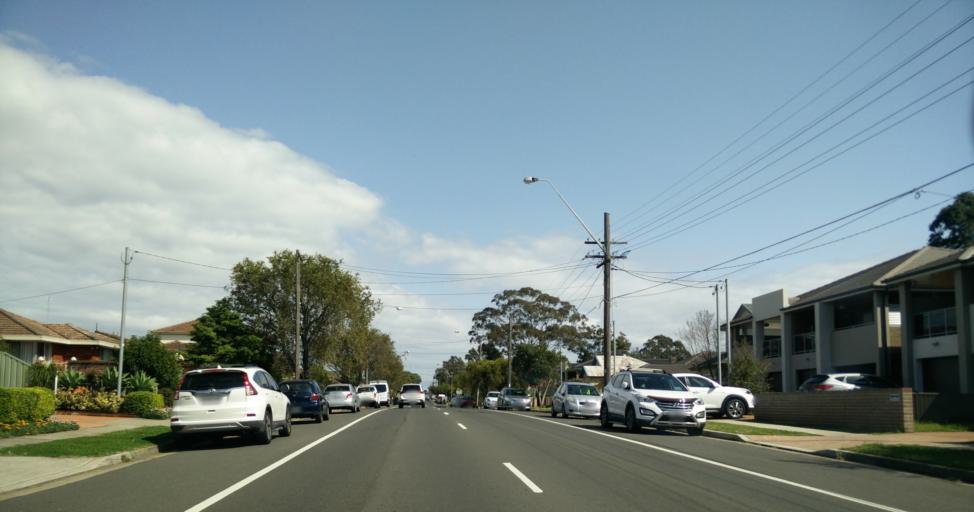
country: AU
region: New South Wales
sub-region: Bankstown
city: Revesby
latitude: -33.9578
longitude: 151.0107
